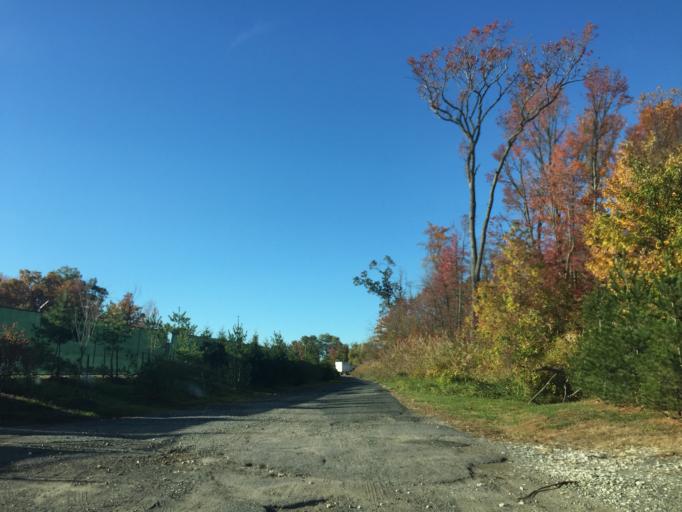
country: US
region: Maryland
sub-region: Baltimore County
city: Rosedale
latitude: 39.3201
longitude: -76.4965
